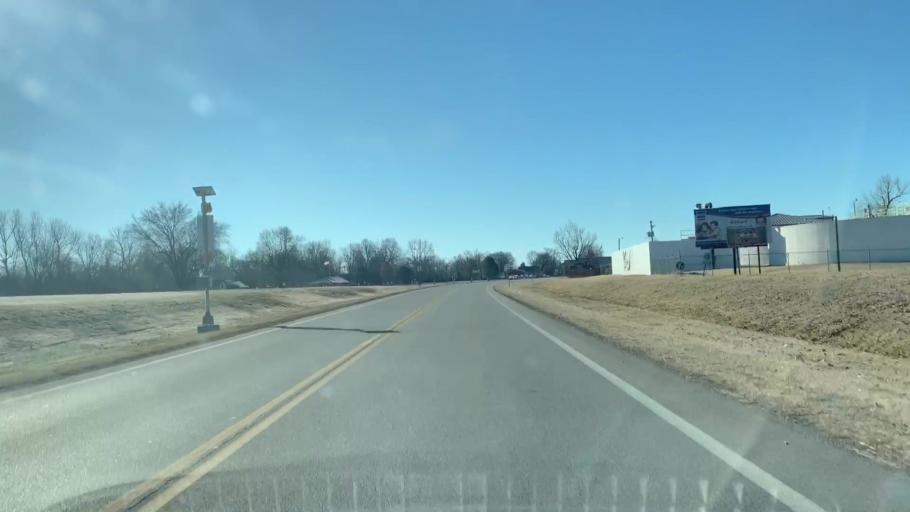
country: US
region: Kansas
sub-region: Cherokee County
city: Baxter Springs
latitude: 37.0363
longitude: -94.7350
